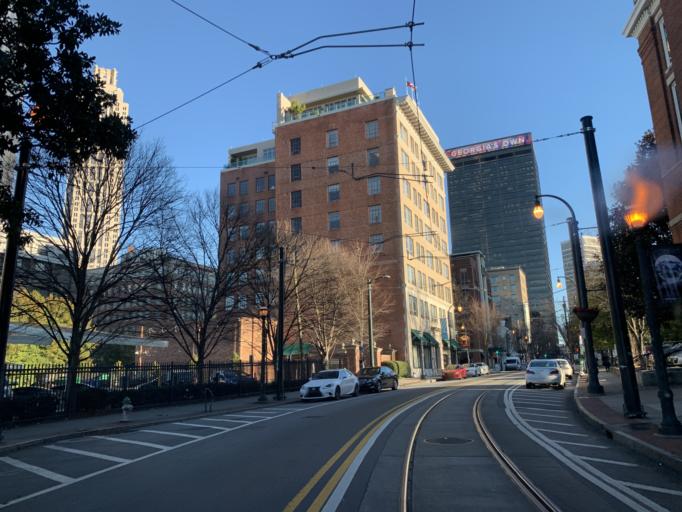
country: US
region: Georgia
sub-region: Fulton County
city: Atlanta
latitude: 33.7590
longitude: -84.3913
